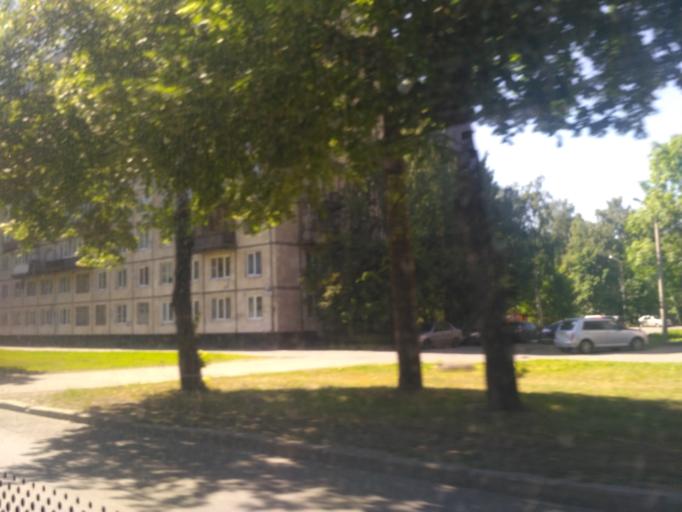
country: RU
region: Leningrad
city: Kalininskiy
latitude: 59.9668
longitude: 30.4142
